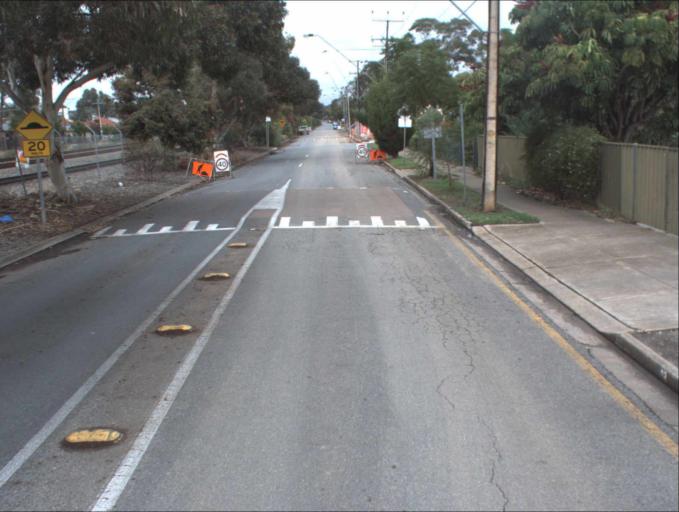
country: AU
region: South Australia
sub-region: Prospect
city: Prospect
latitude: -34.8883
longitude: 138.5833
